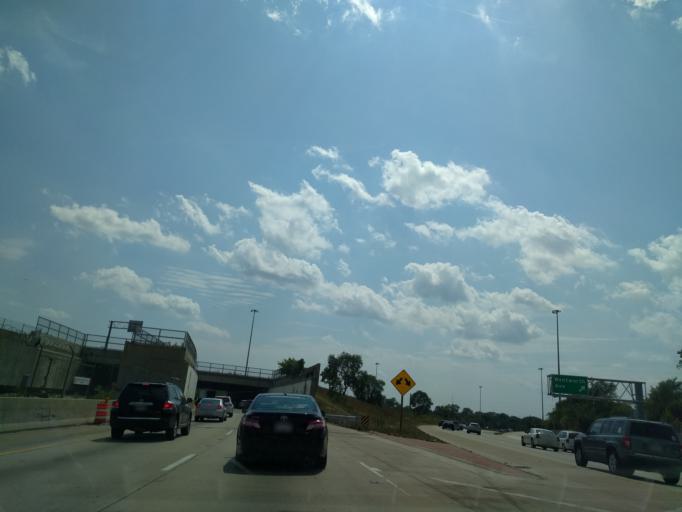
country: US
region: Illinois
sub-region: Cook County
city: Calumet Park
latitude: 41.7191
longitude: -87.6249
